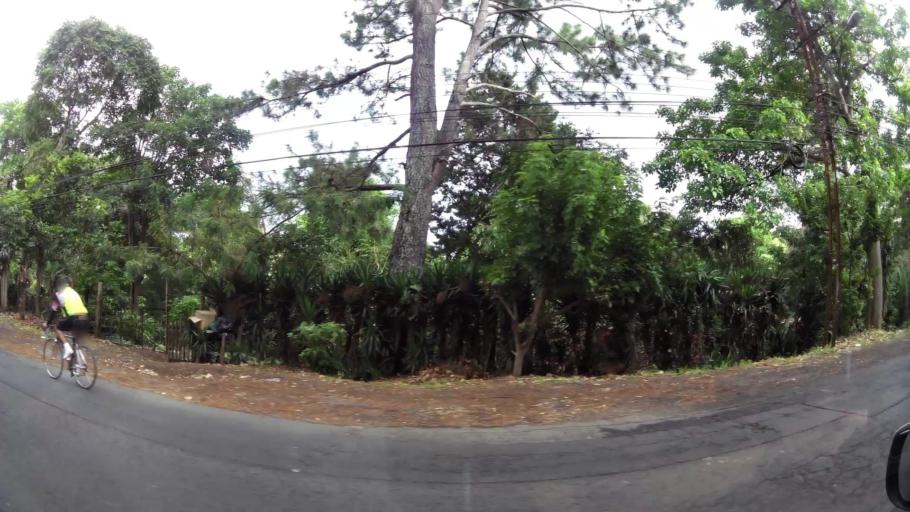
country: CR
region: San Jose
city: Curridabat
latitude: 9.9096
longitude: -84.0381
